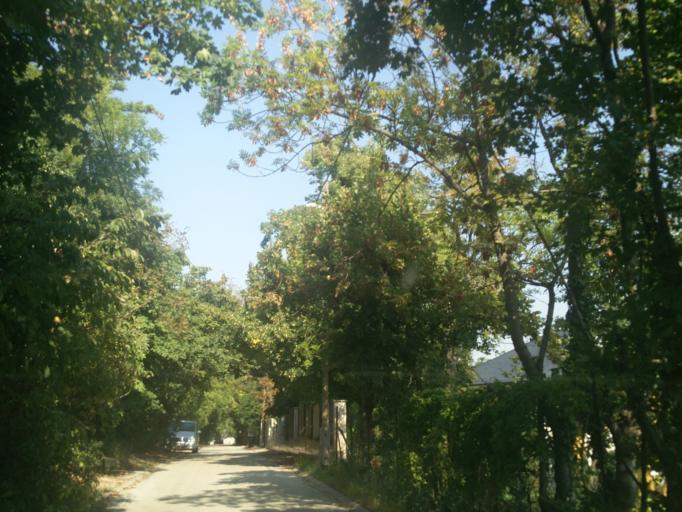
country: HU
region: Budapest
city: Budapest XII. keruelet
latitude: 47.5026
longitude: 18.9940
